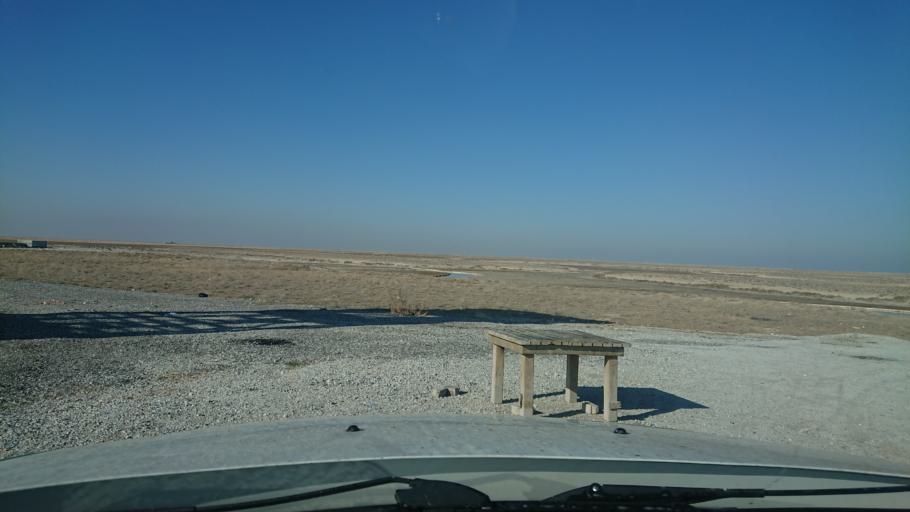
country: TR
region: Aksaray
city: Eskil
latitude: 38.4251
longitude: 33.5016
